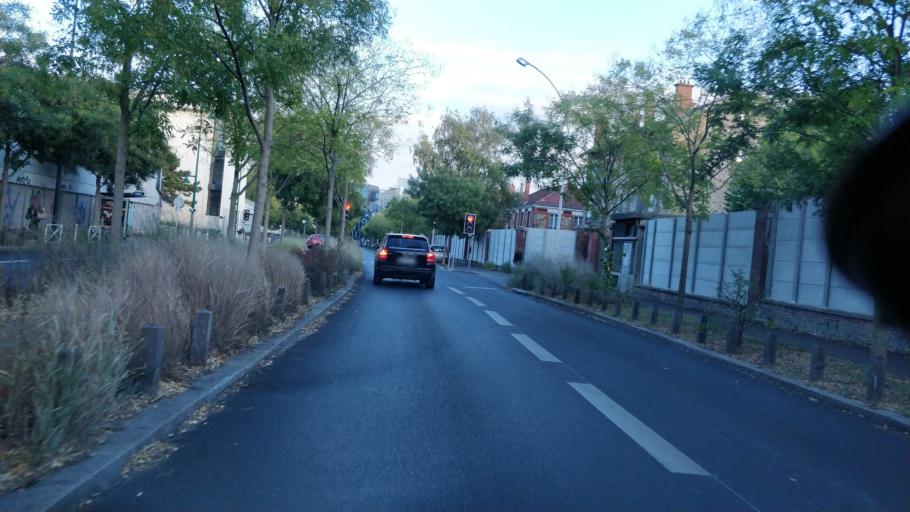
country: FR
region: Ile-de-France
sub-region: Departement des Hauts-de-Seine
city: Montrouge
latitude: 48.8097
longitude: 2.3216
